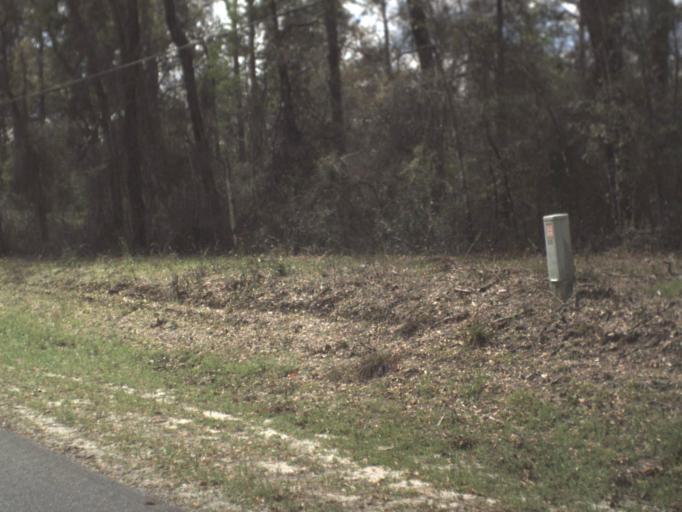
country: US
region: Florida
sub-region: Wakulla County
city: Crawfordville
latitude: 30.1543
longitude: -84.3825
